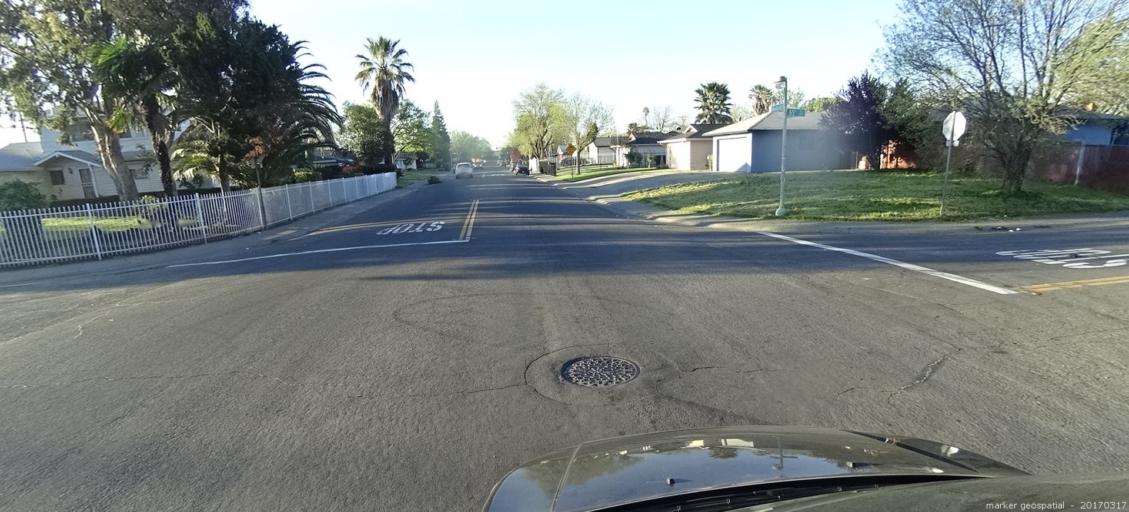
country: US
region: California
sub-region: Sacramento County
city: Parkway
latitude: 38.4933
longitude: -121.4867
